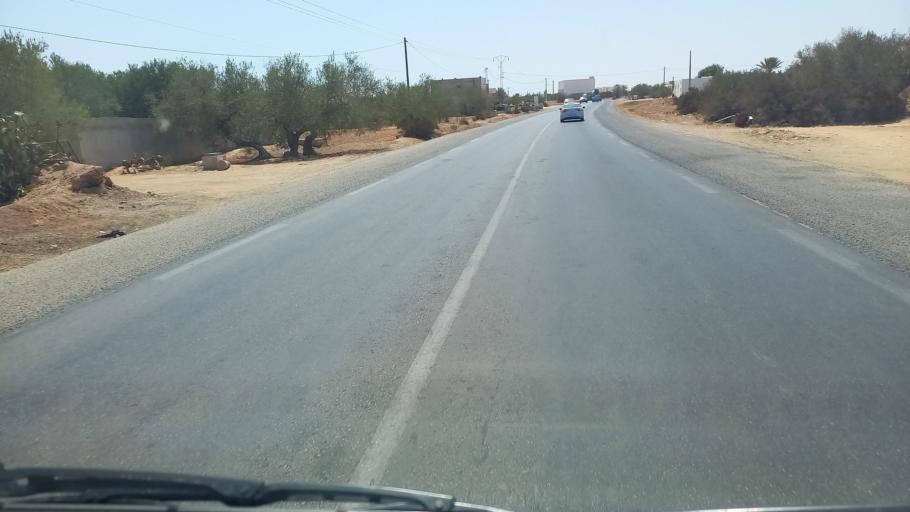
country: TN
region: Madanin
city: Houmt Souk
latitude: 33.8206
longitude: 10.8711
